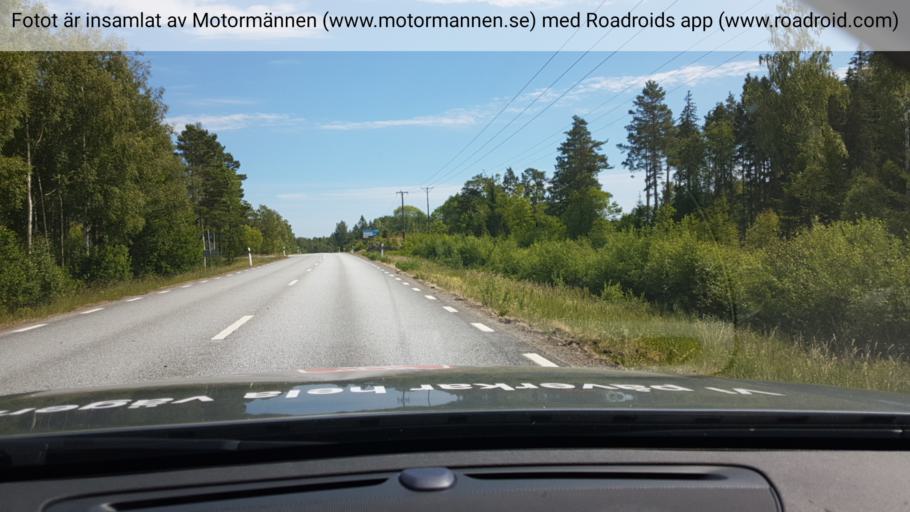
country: SE
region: Uppsala
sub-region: Osthammars Kommun
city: Anneberg
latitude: 60.1680
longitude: 18.4483
